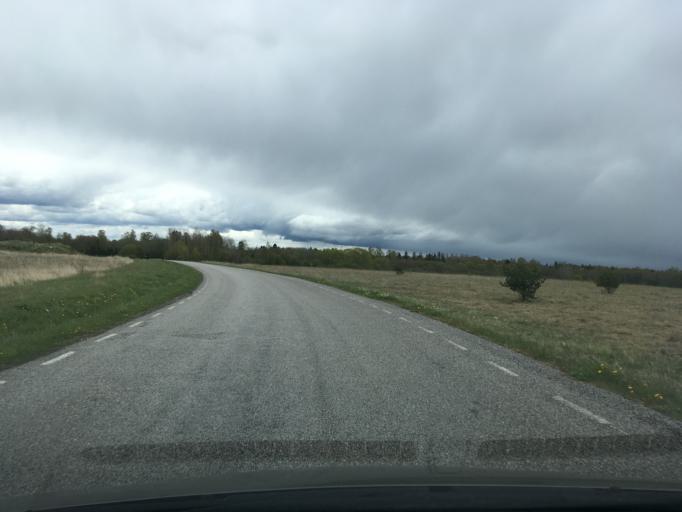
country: EE
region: Harju
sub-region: Rae vald
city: Vaida
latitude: 59.3535
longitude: 24.9872
